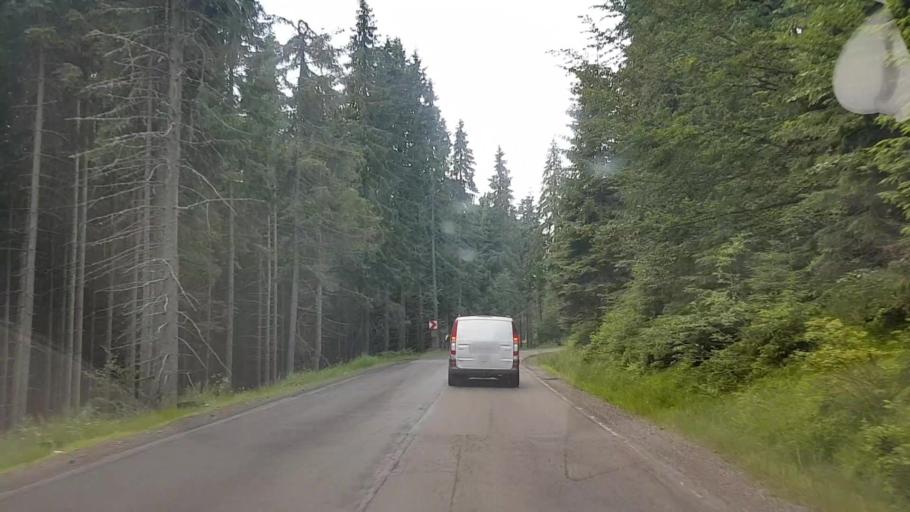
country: RO
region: Harghita
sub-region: Comuna Varsag
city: Varsag
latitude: 46.6595
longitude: 25.3011
